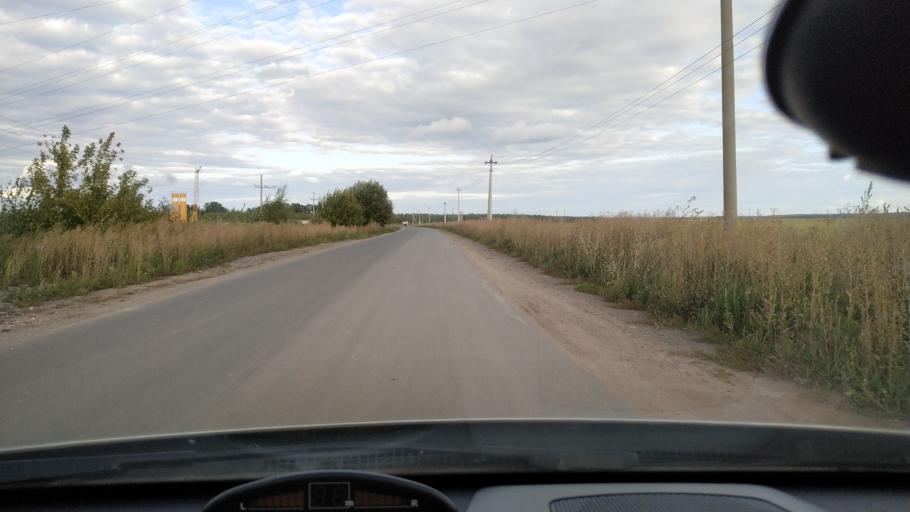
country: RU
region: Rjazan
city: Polyany
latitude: 54.5767
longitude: 39.8454
